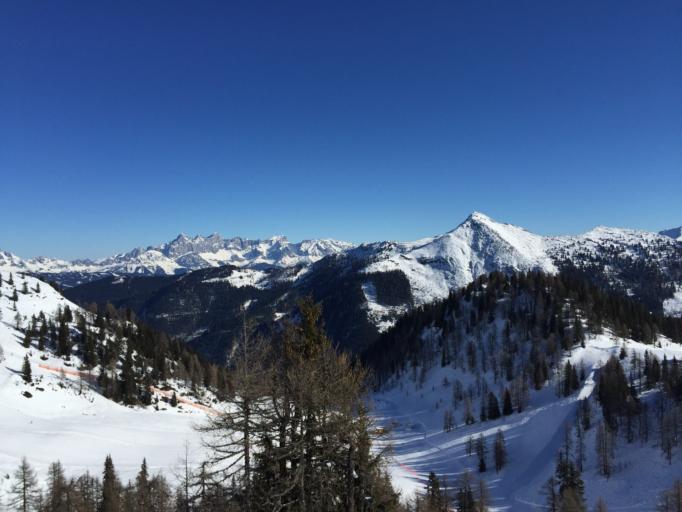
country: AT
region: Salzburg
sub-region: Politischer Bezirk Sankt Johann im Pongau
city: Flachau
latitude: 47.2948
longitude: 13.4296
